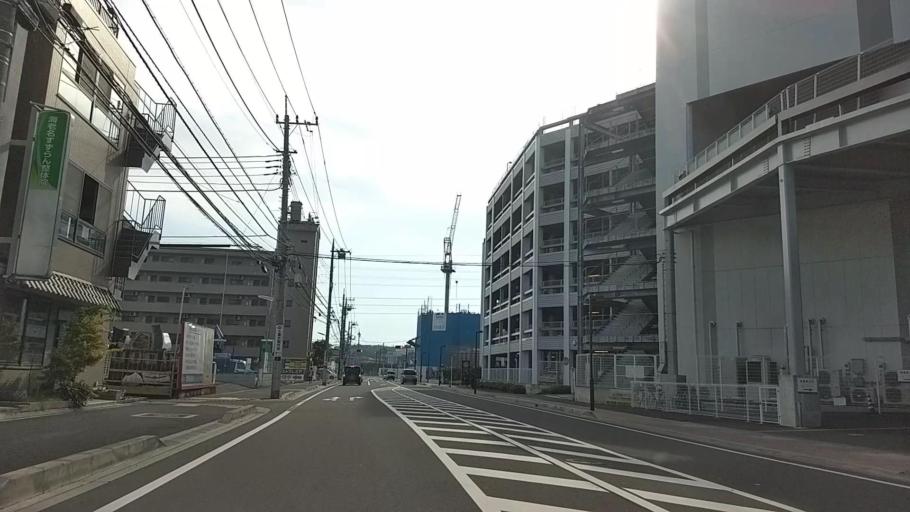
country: JP
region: Kanagawa
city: Zama
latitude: 35.4575
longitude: 139.3891
